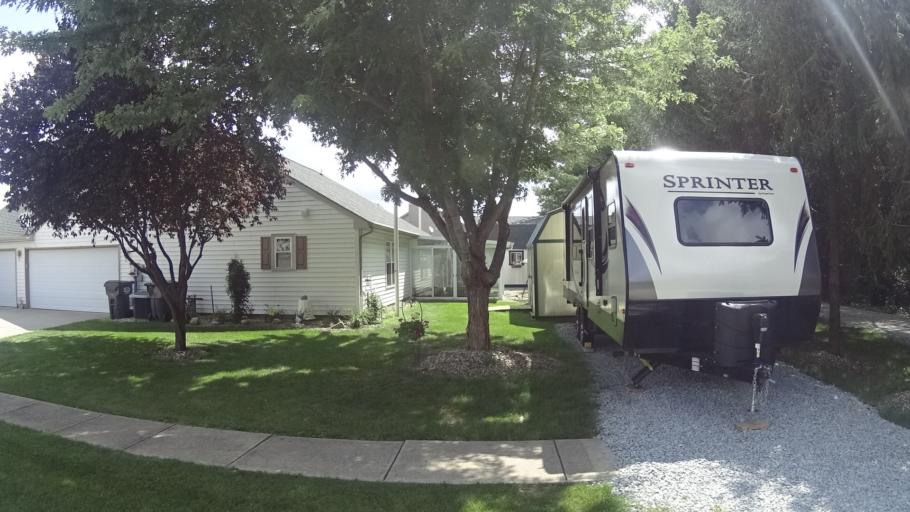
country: US
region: Indiana
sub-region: Madison County
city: Pendleton
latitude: 40.0101
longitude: -85.7484
